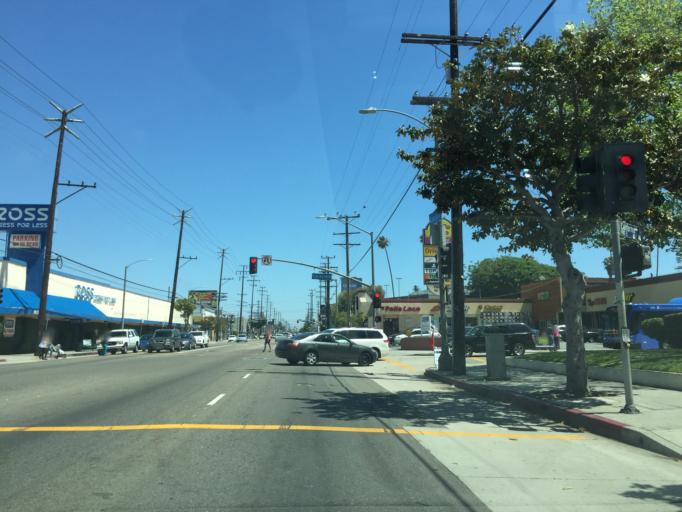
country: US
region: California
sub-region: Los Angeles County
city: Marina del Rey
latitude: 33.9981
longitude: -118.4613
